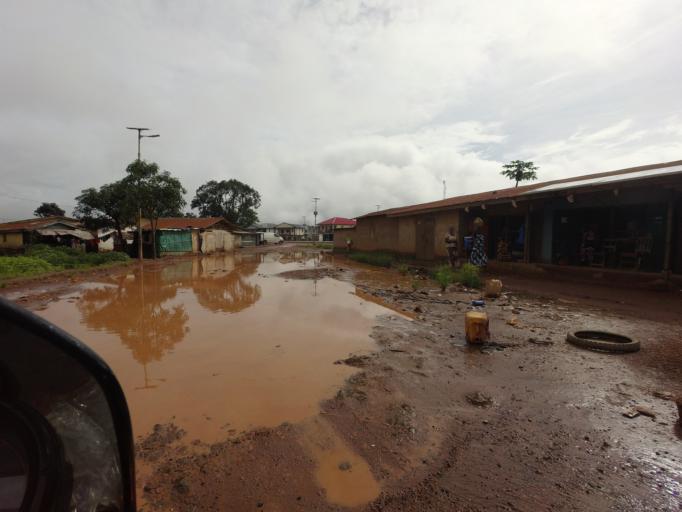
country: SL
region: Northern Province
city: Kambia
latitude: 9.1084
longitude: -12.9253
